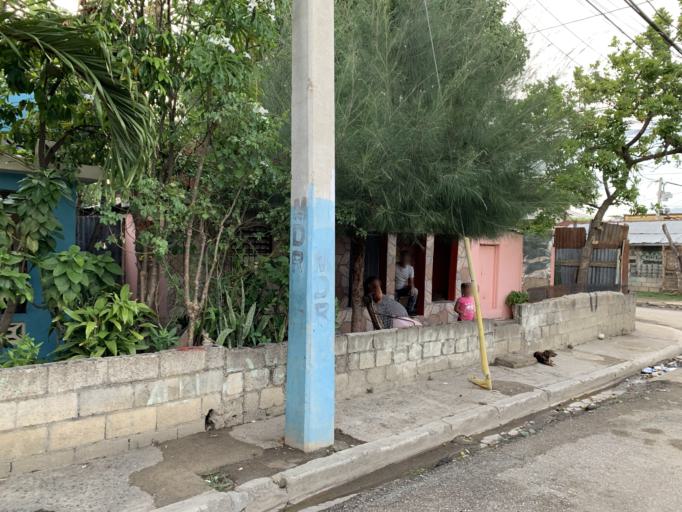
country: DO
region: Santiago
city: Palmar Arriba
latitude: 19.4864
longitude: -70.7466
